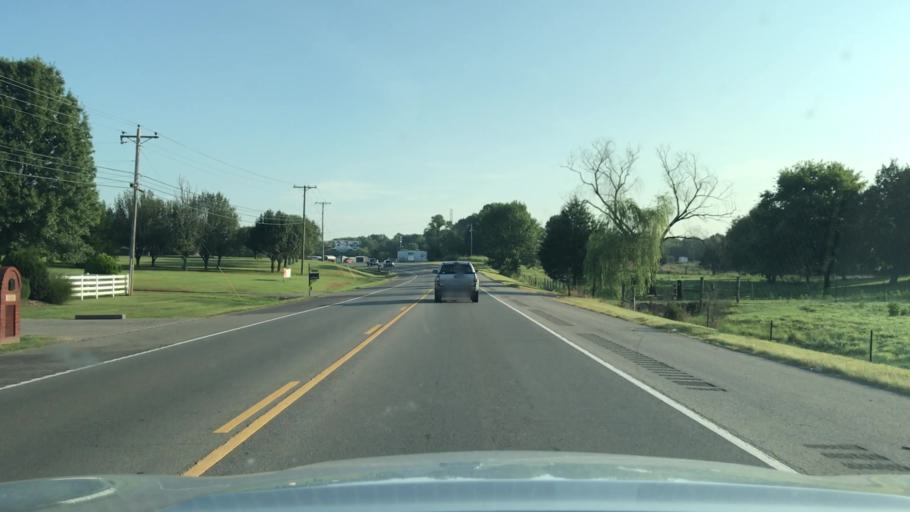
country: US
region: Tennessee
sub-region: Wilson County
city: Rural Hill
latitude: 36.1490
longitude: -86.5157
